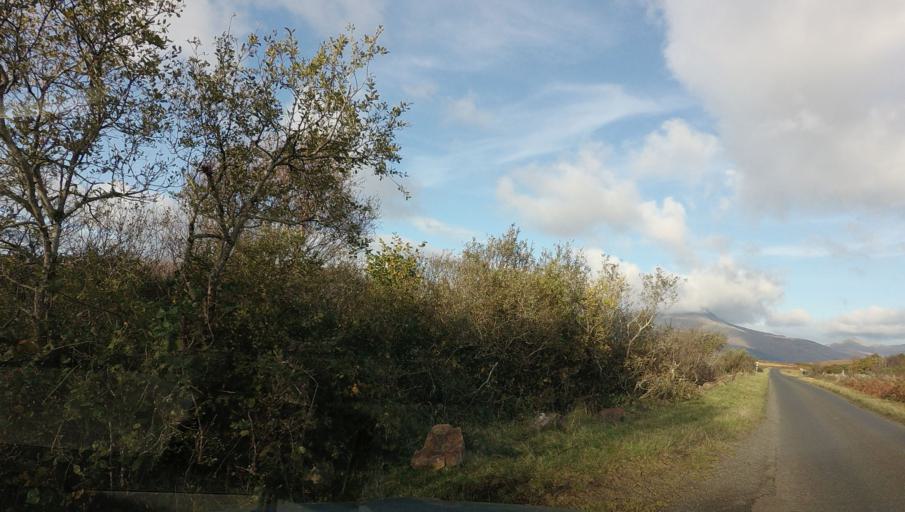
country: GB
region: Scotland
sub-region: Argyll and Bute
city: Isle Of Mull
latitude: 56.3428
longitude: -6.1019
